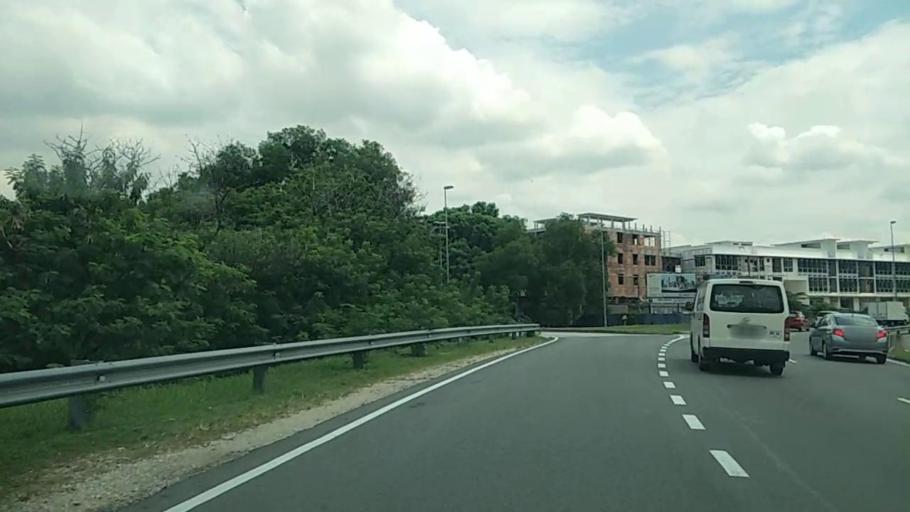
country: MY
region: Selangor
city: Subang Jaya
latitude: 2.9892
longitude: 101.6181
